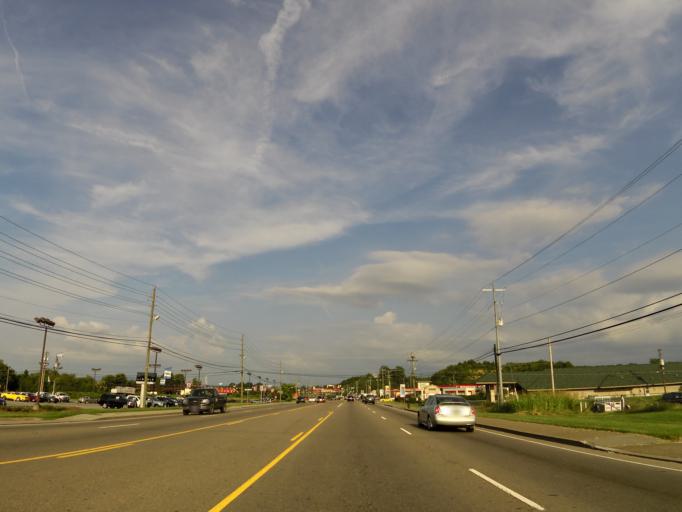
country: US
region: Tennessee
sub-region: Sevier County
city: Sevierville
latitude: 35.8651
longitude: -83.5491
